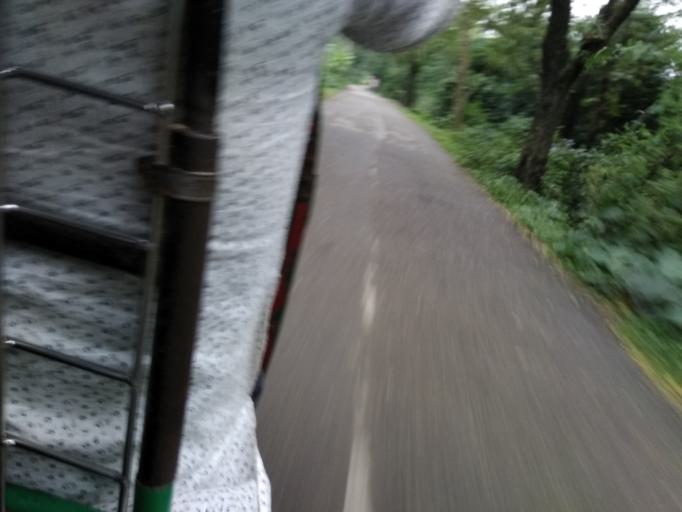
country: BD
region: Chittagong
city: Chhagalnaiya
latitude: 22.8144
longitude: 91.4991
